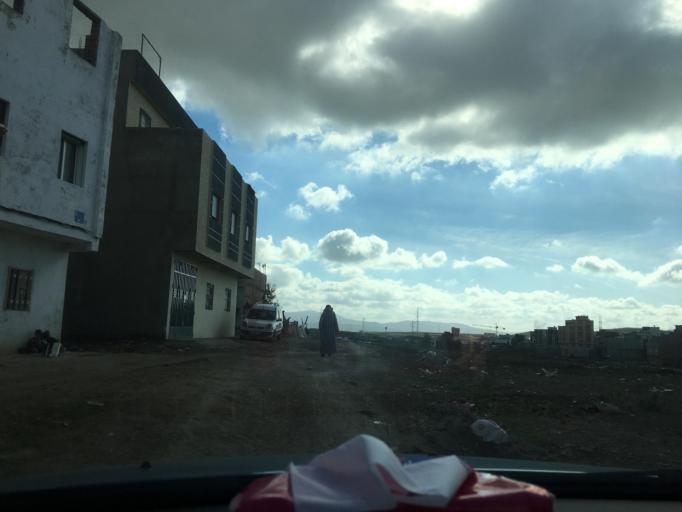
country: MA
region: Tanger-Tetouan
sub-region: Tanger-Assilah
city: Tangier
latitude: 35.7141
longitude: -5.8135
